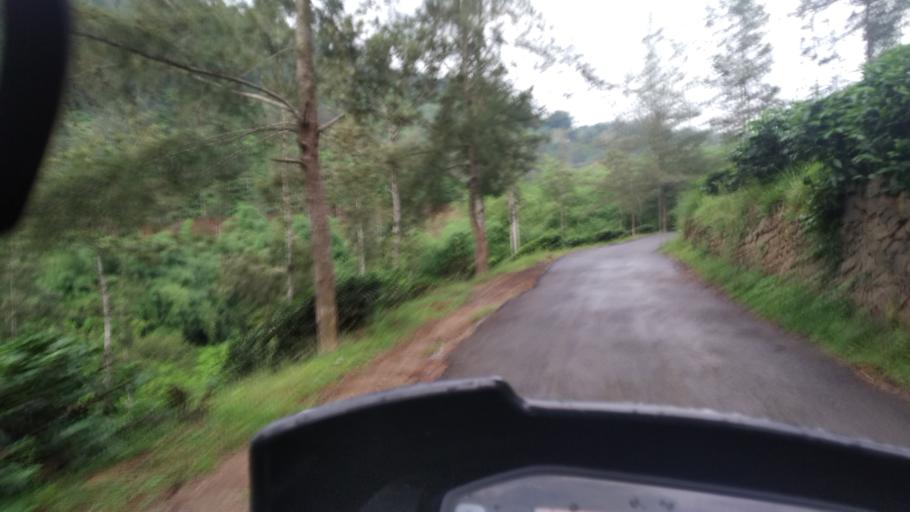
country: IN
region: Tamil Nadu
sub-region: Theni
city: Gudalur
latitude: 9.5639
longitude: 77.0773
